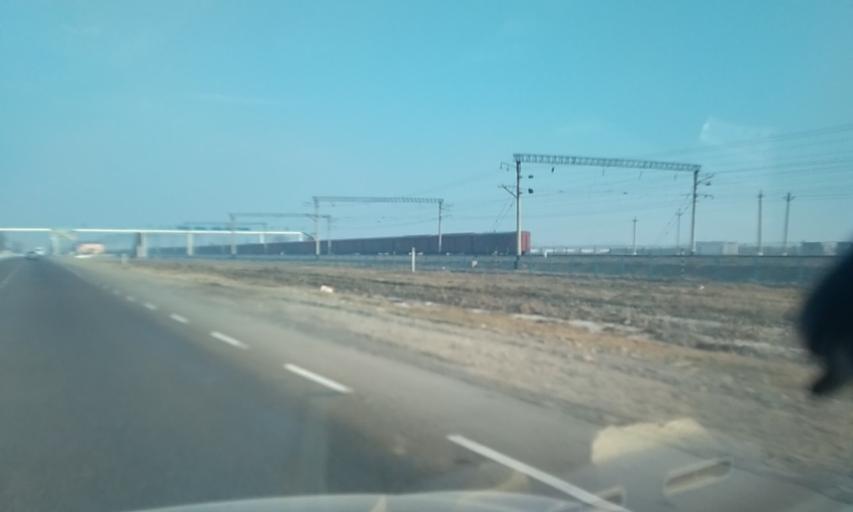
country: UZ
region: Sirdaryo
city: Sirdaryo
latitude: 40.7068
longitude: 68.6995
